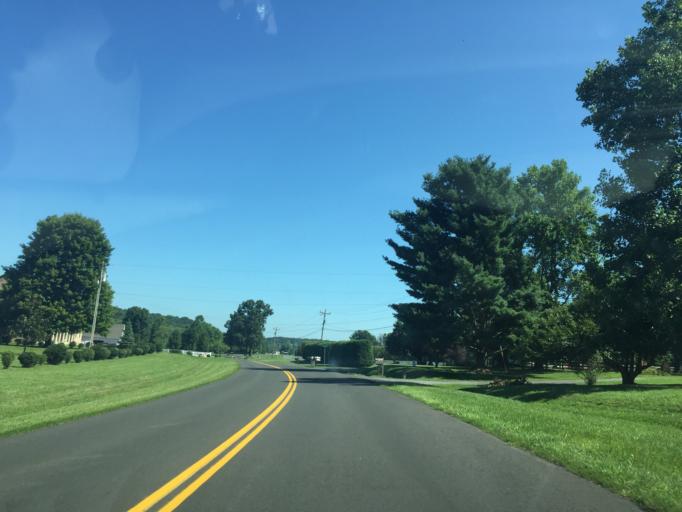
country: US
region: Virginia
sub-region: Warren County
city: Apple Mountain Lake
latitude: 38.9389
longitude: -78.1281
